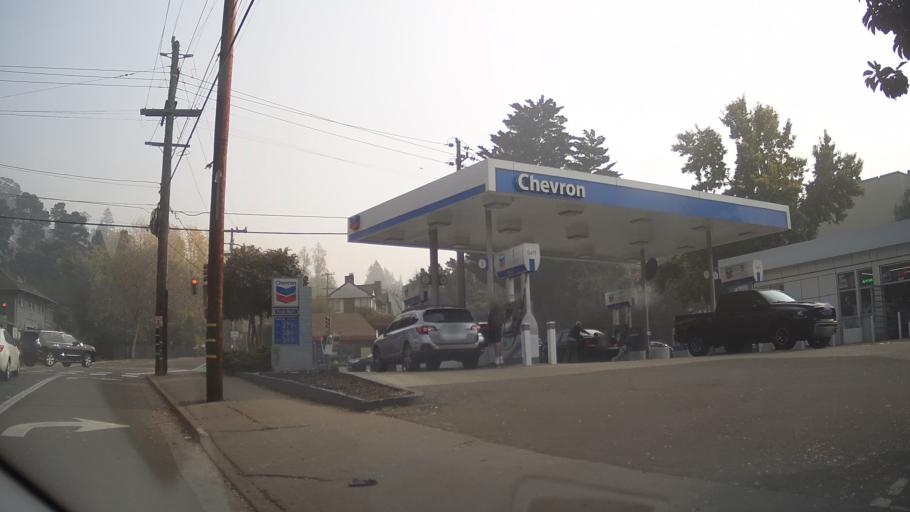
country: US
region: California
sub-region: Alameda County
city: Berkeley
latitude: 37.8583
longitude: -122.2447
